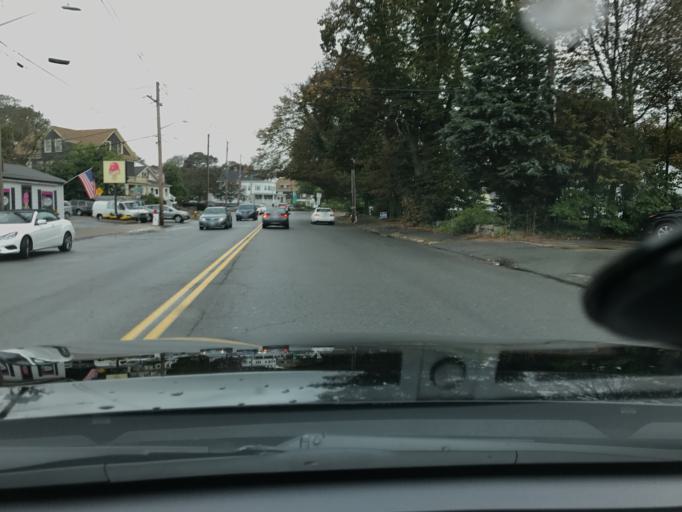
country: US
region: Massachusetts
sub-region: Essex County
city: Peabody
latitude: 42.5355
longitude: -70.9168
